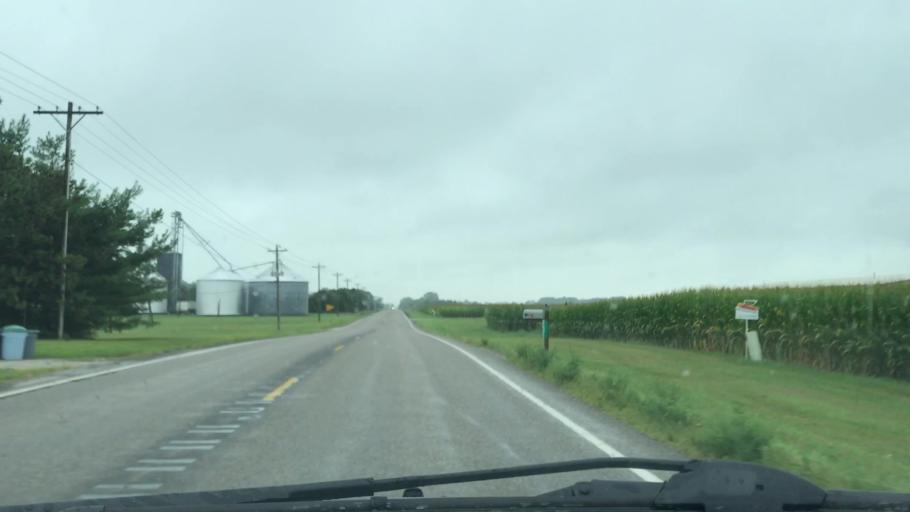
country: US
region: Indiana
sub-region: Boone County
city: Lebanon
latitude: 40.1265
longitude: -86.4192
